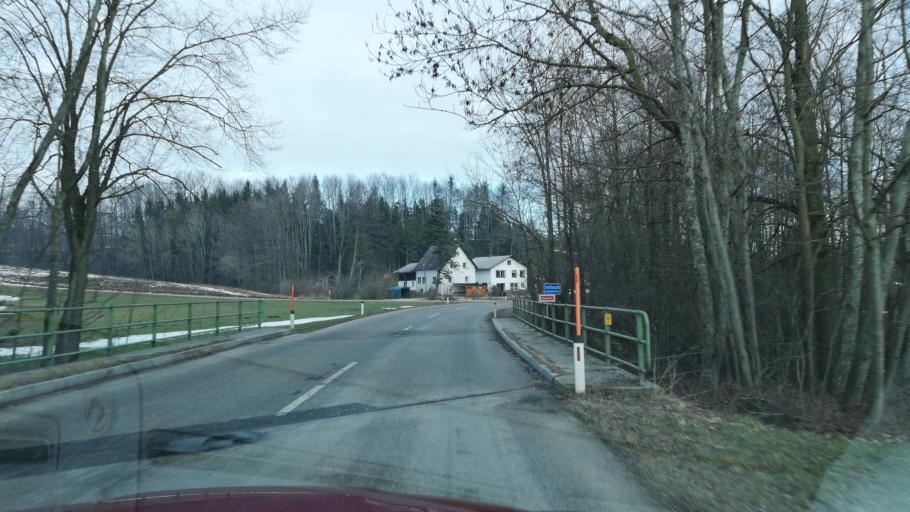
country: AT
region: Upper Austria
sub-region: Politischer Bezirk Vocklabruck
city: Wolfsegg am Hausruck
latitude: 48.1664
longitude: 13.6763
